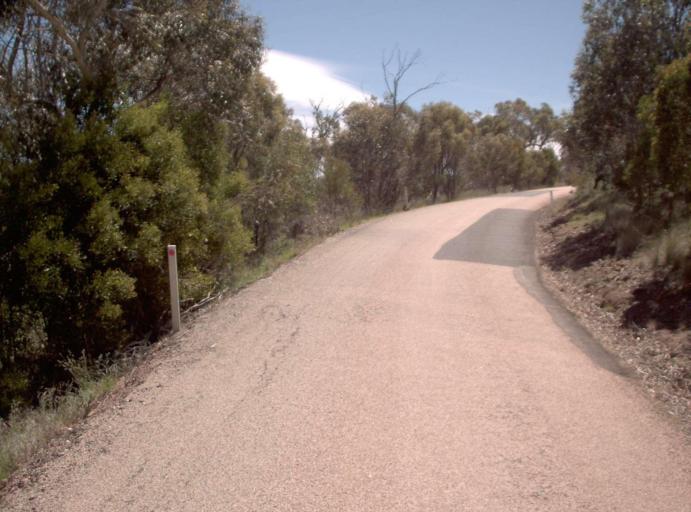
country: AU
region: New South Wales
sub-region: Snowy River
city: Jindabyne
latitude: -37.1026
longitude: 148.2506
